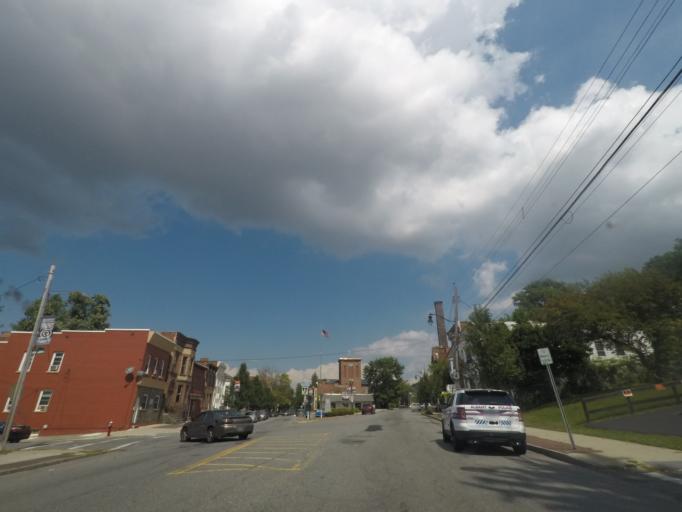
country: US
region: New York
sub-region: Rensselaer County
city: Troy
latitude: 42.7141
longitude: -73.6940
